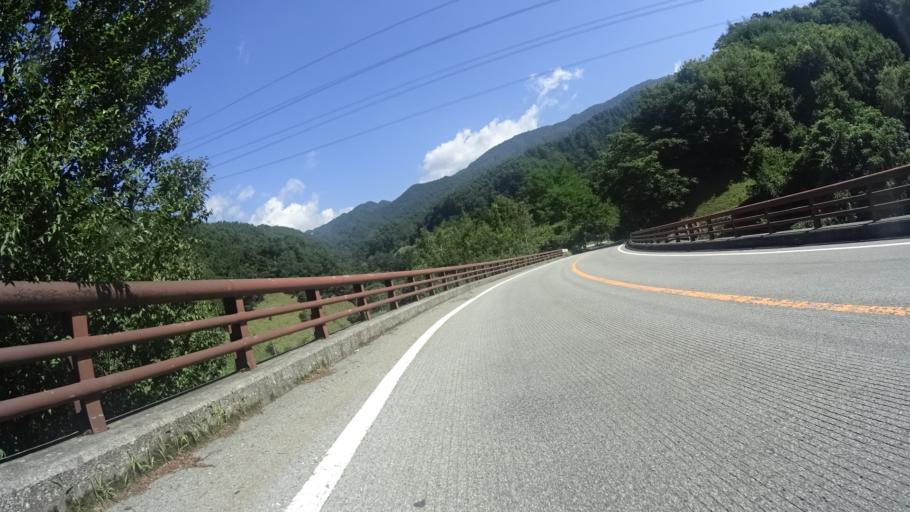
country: JP
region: Yamanashi
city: Enzan
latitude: 35.7416
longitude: 138.8073
